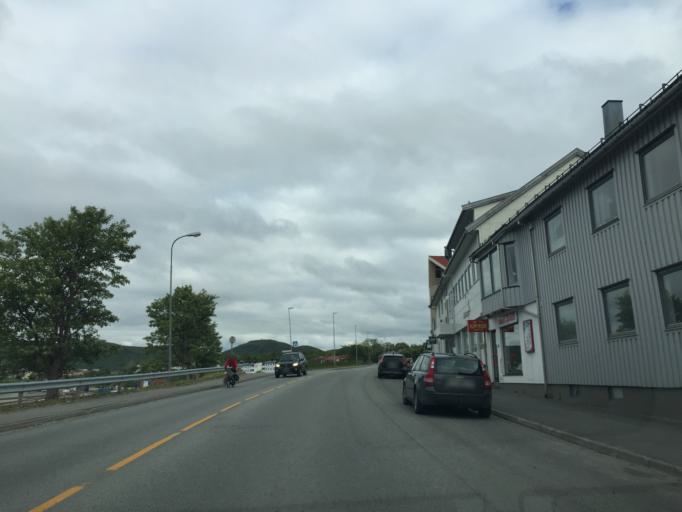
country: NO
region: Nordland
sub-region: Bodo
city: Bodo
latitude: 67.2862
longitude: 14.3935
